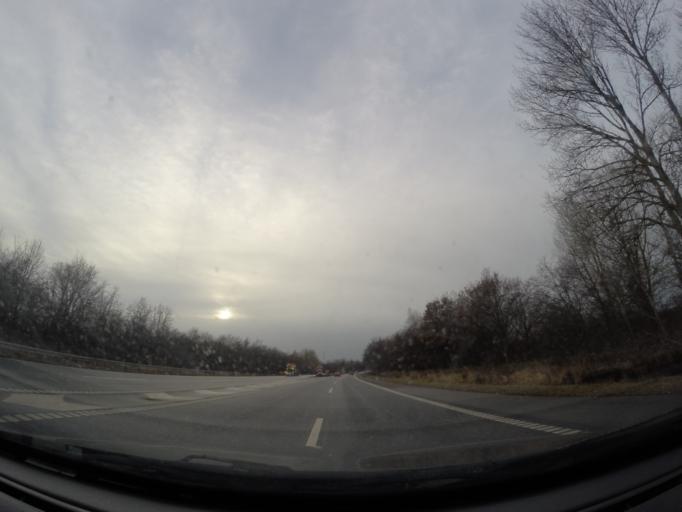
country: DK
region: Capital Region
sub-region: Hoje-Taastrup Kommune
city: Taastrup
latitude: 55.6695
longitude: 12.3169
